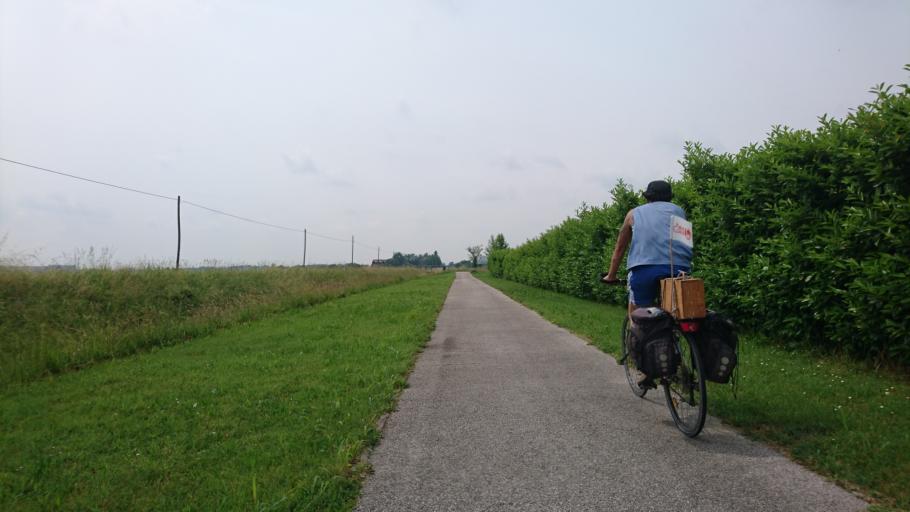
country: IT
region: Veneto
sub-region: Provincia di Padova
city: Vighizzolo d'Este
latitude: 45.1271
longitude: 11.6249
